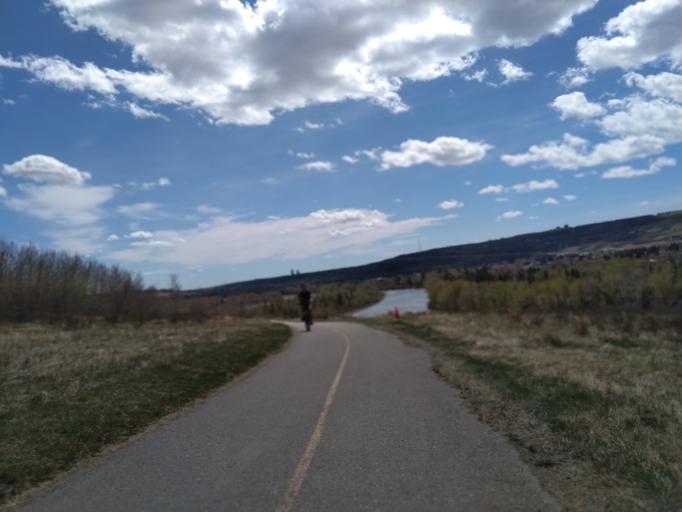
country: CA
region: Alberta
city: Calgary
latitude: 51.0984
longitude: -114.1902
